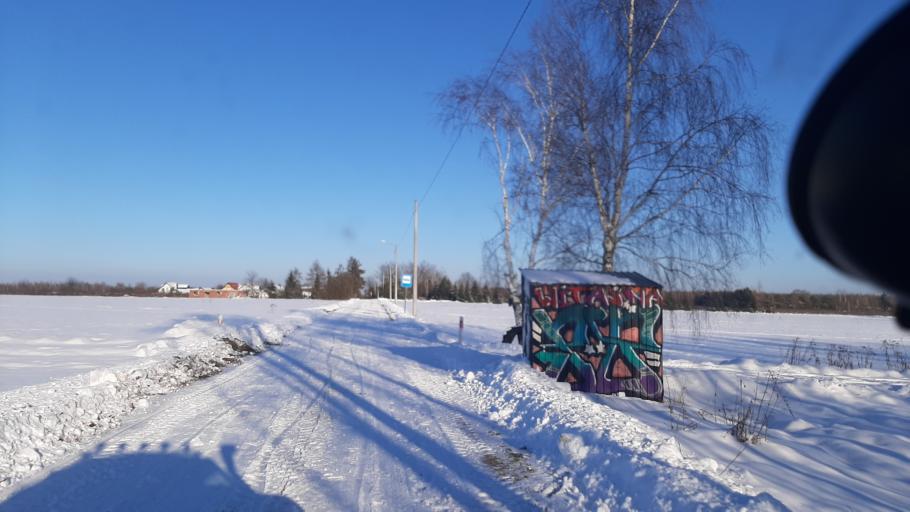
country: PL
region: Lublin Voivodeship
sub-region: Powiat lubelski
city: Jastkow
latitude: 51.3894
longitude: 22.4370
